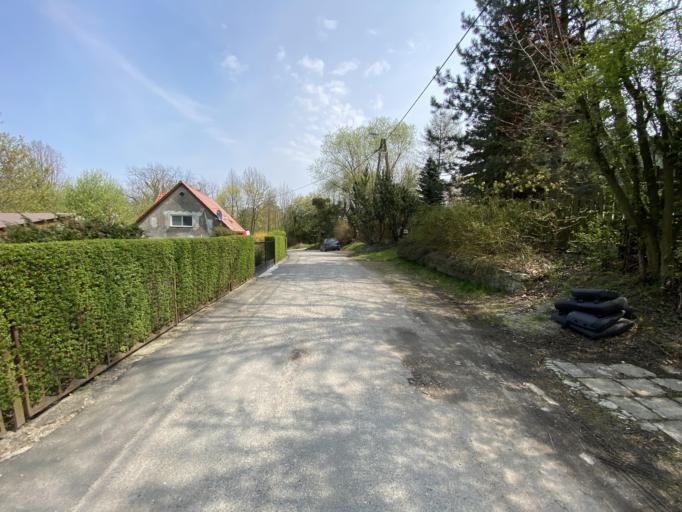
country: PL
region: Lower Silesian Voivodeship
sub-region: Powiat wroclawski
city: Sobotka
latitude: 50.8444
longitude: 16.7297
